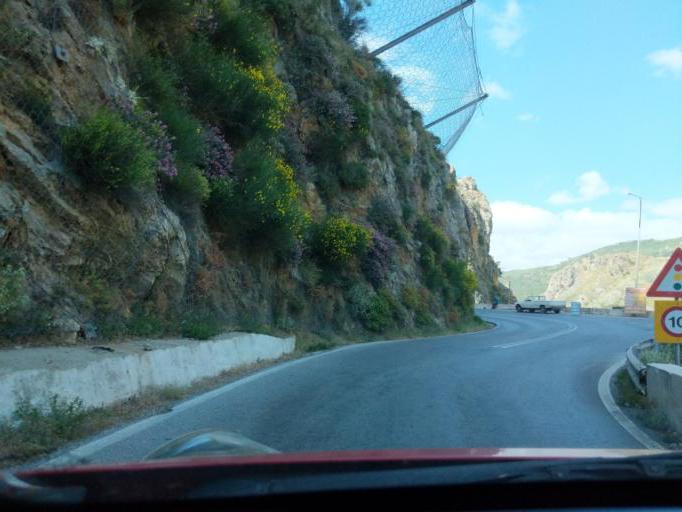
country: GR
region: Crete
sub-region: Nomos Chanias
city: Kissamos
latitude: 35.4149
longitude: 23.6850
